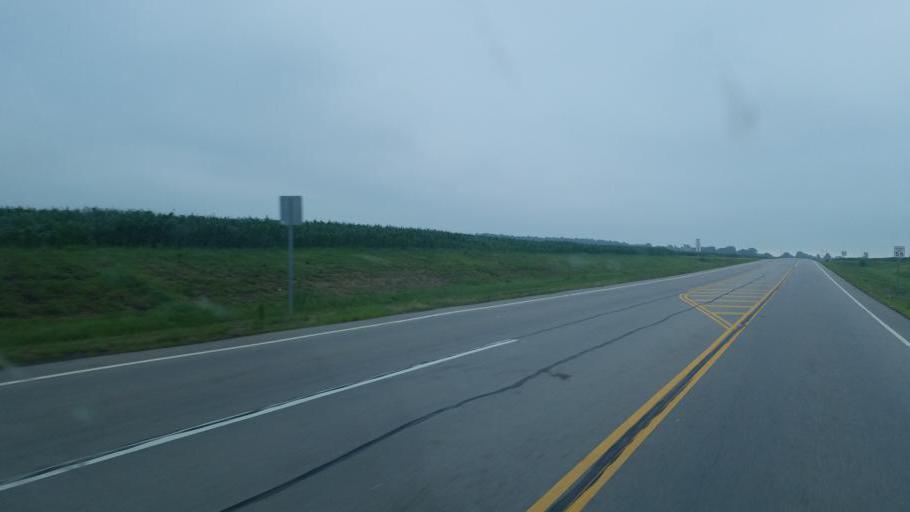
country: US
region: Ohio
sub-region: Fayette County
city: Washington Court House
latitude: 39.5632
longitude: -83.4067
